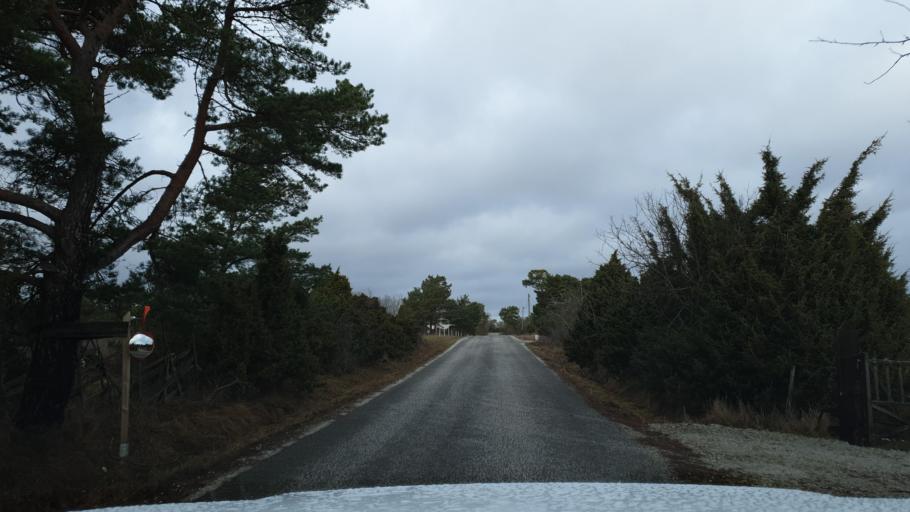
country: SE
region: Gotland
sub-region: Gotland
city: Slite
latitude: 57.3877
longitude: 18.8086
